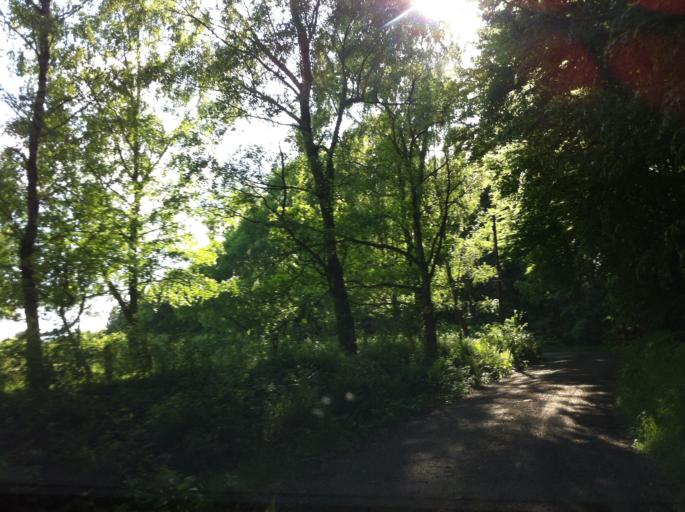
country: SE
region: Skane
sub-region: Klippans Kommun
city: Ljungbyhed
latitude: 56.0416
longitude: 13.2209
